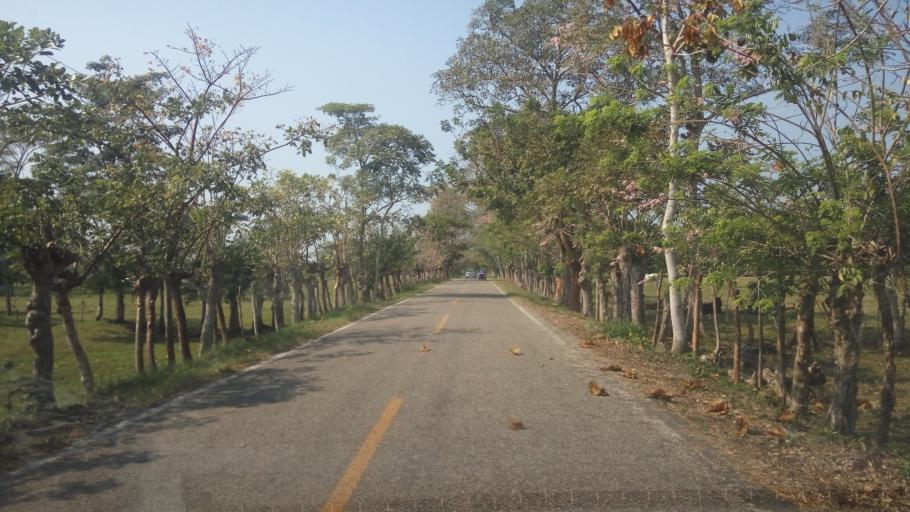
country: MX
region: Tabasco
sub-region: Centla
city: Alvaro Obregon 2da. Seccion (El Lechugal)
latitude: 18.4682
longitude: -92.7624
